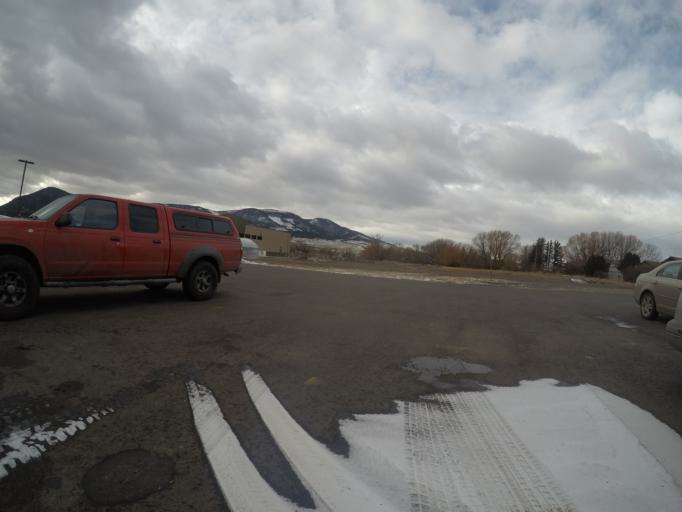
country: US
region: Montana
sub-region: Park County
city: Livingston
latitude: 45.6397
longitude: -110.5757
